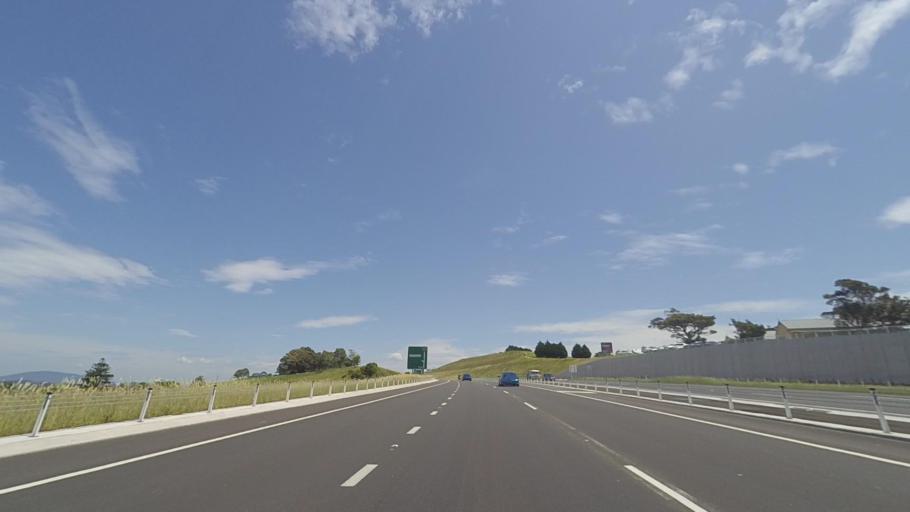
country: AU
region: New South Wales
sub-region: Kiama
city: Gerringong
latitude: -34.7458
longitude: 150.8083
